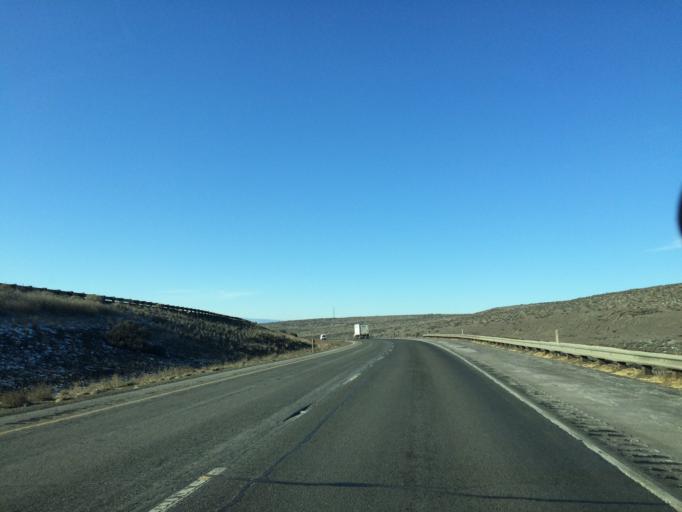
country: US
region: Washington
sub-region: Kittitas County
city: Kittitas
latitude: 46.9494
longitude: -120.2537
